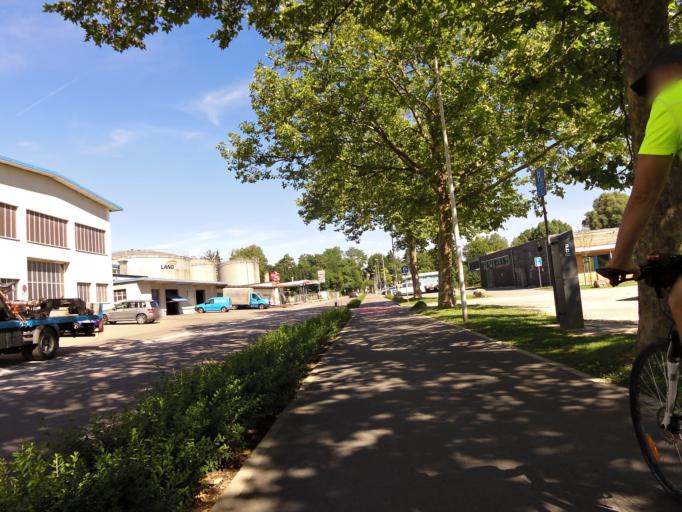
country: CH
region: Thurgau
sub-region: Kreuzlingen District
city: Kreuzlingen
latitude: 47.6524
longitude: 9.1795
